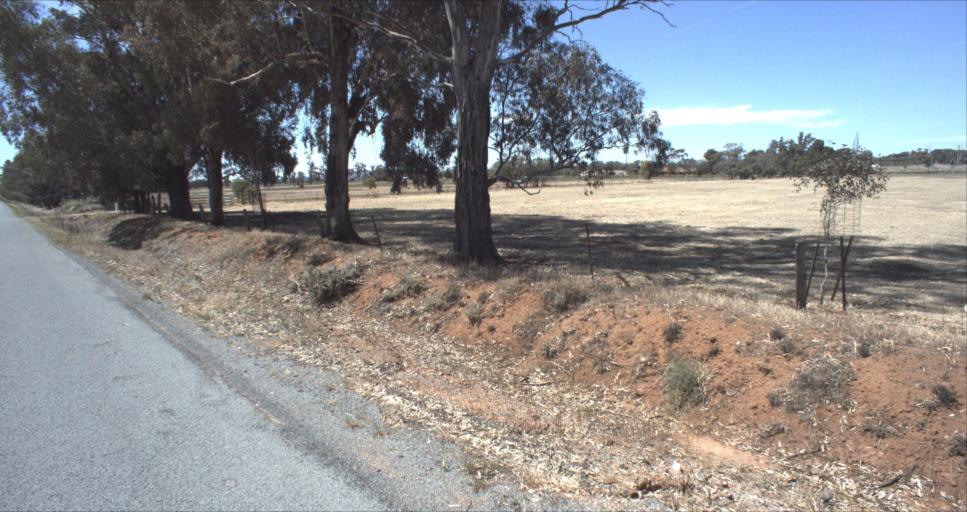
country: AU
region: New South Wales
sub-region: Leeton
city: Leeton
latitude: -34.5781
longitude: 146.4210
